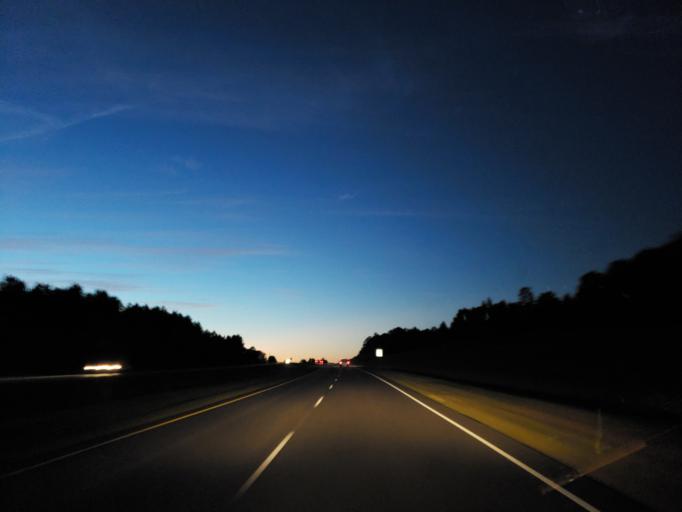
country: US
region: Mississippi
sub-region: Clarke County
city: Quitman
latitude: 32.1031
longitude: -88.7082
